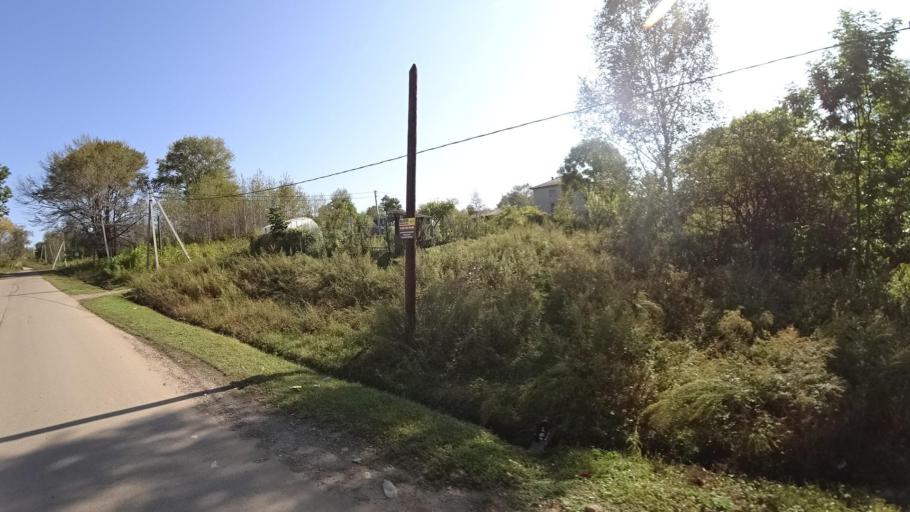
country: RU
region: Jewish Autonomous Oblast
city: Bira
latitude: 49.0034
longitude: 132.4655
